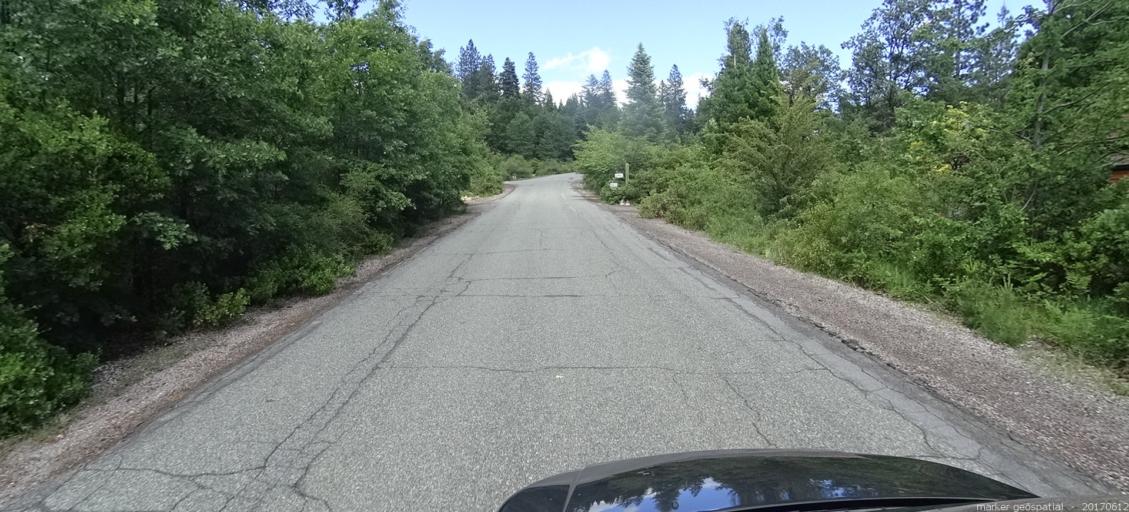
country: US
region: California
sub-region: Siskiyou County
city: Mount Shasta
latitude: 41.3142
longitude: -122.2849
